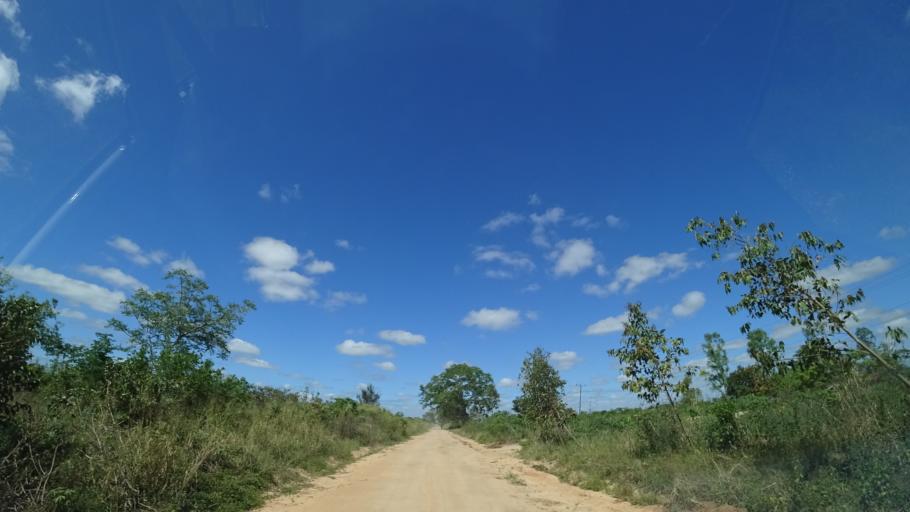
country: MZ
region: Sofala
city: Dondo
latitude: -19.2853
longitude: 34.6862
